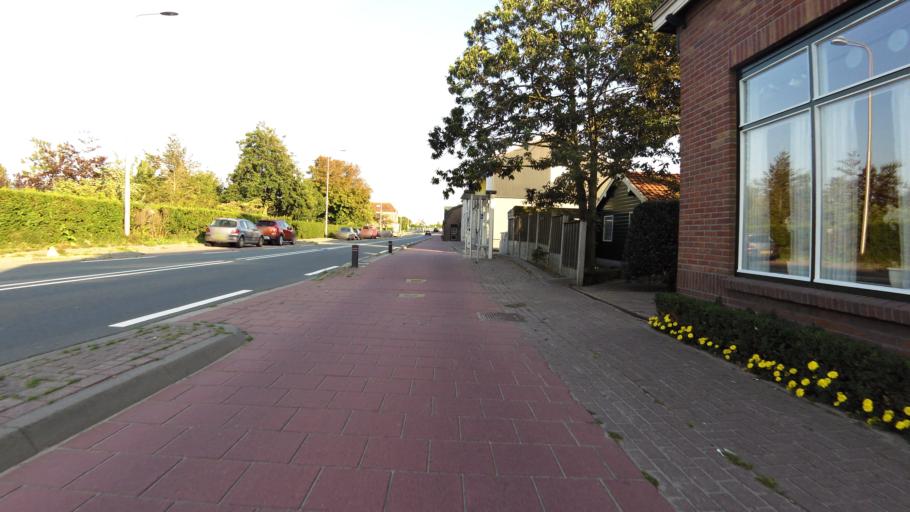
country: NL
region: South Holland
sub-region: Gemeente Noordwijkerhout
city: Noordwijkerhout
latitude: 52.2459
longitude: 4.4936
